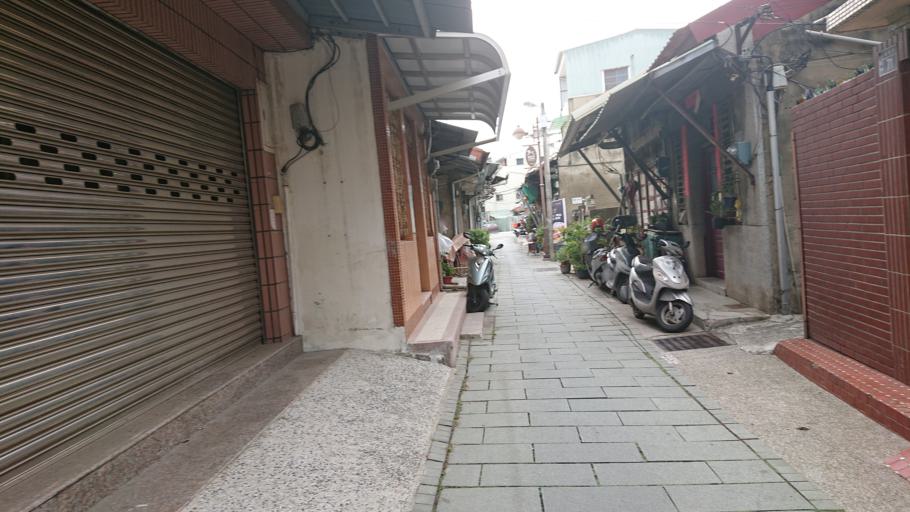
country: TW
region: Taiwan
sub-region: Tainan
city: Tainan
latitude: 23.0007
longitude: 120.2029
